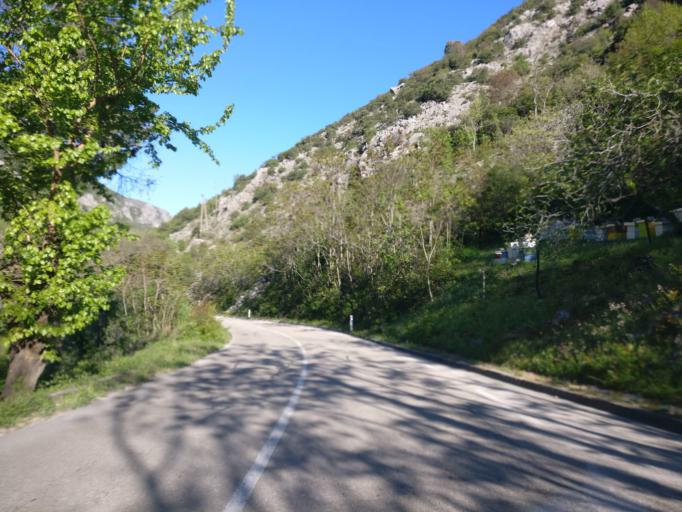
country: BA
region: Federation of Bosnia and Herzegovina
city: Stolac
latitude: 43.0725
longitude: 18.0374
